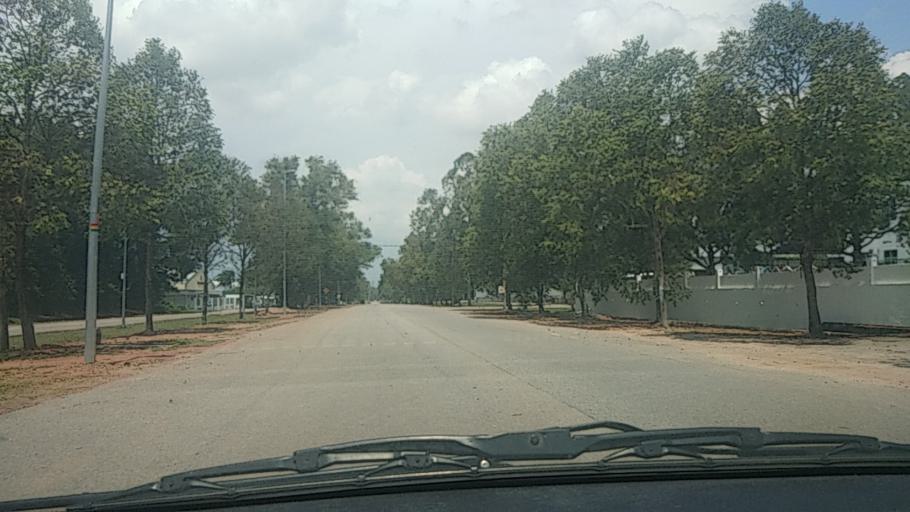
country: MY
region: Kedah
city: Sungai Petani
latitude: 5.6531
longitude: 100.5314
